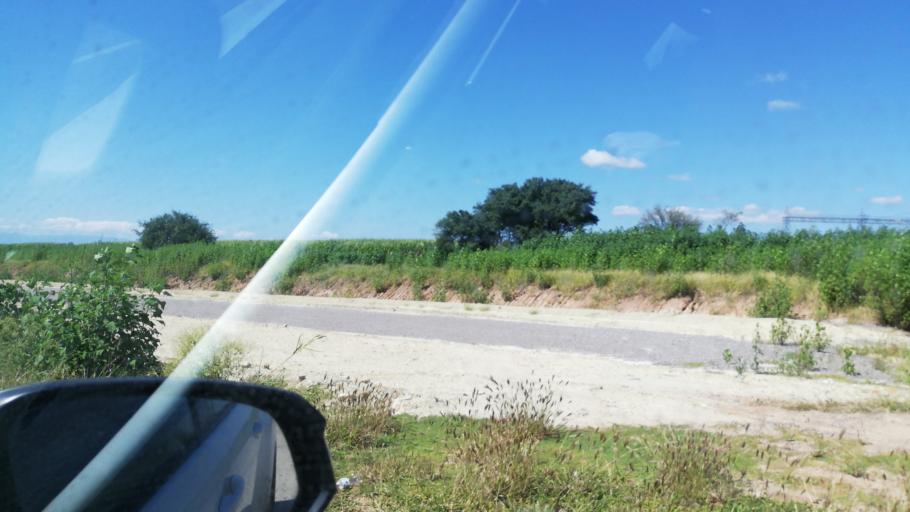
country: AR
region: Jujuy
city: La Mendieta
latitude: -24.3746
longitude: -64.9974
